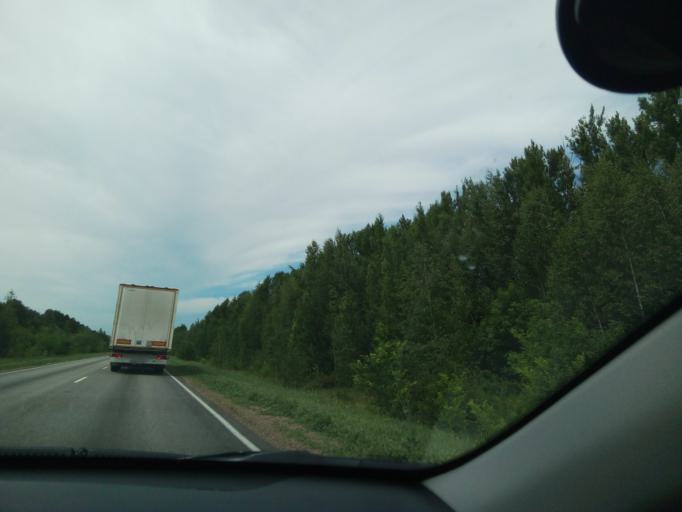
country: RU
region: Tambov
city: Zavoronezhskoye
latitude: 52.6199
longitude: 40.8297
